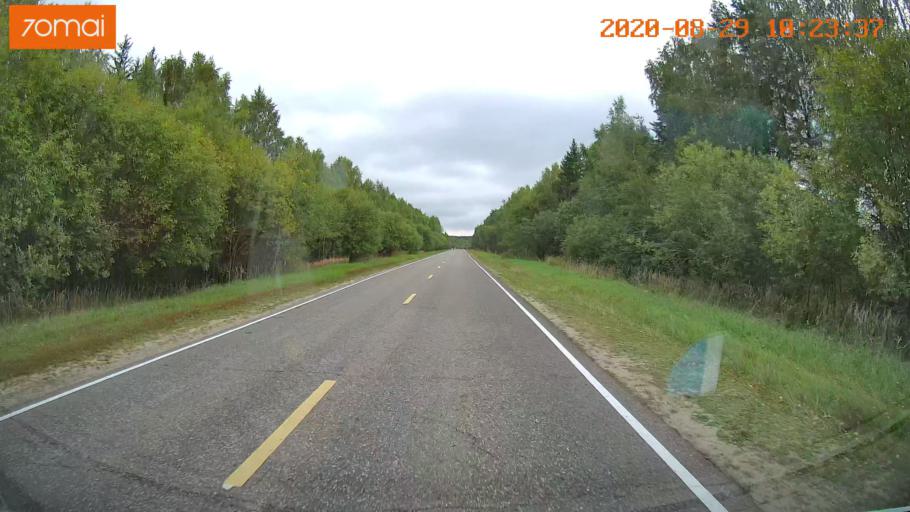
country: RU
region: Ivanovo
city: Yur'yevets
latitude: 57.3234
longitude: 42.9778
